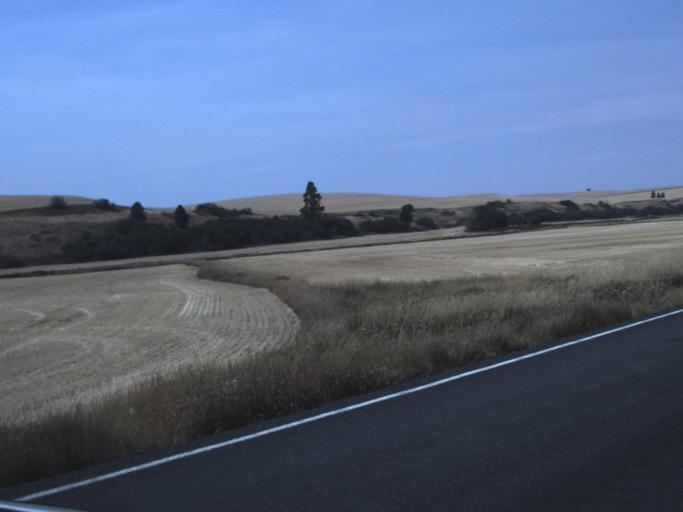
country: US
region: Idaho
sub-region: Benewah County
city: Plummer
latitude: 47.3159
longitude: -117.1705
